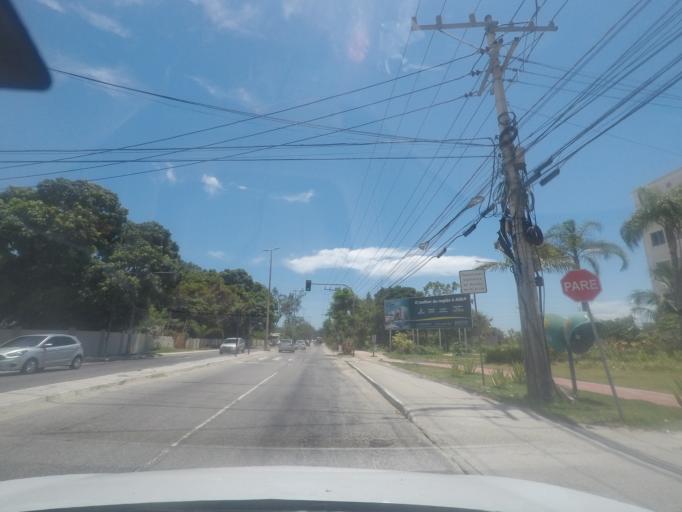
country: BR
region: Rio de Janeiro
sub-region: Itaguai
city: Itaguai
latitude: -22.8997
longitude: -43.6797
